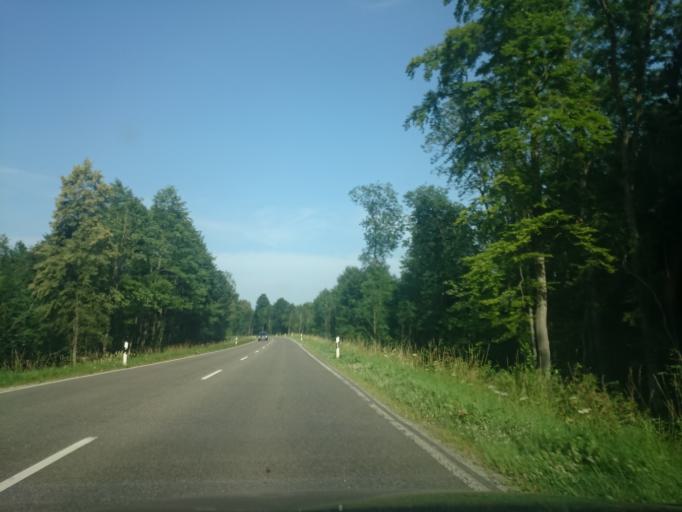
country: DE
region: Bavaria
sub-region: Upper Bavaria
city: Althegnenberg
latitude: 48.2358
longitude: 11.0771
